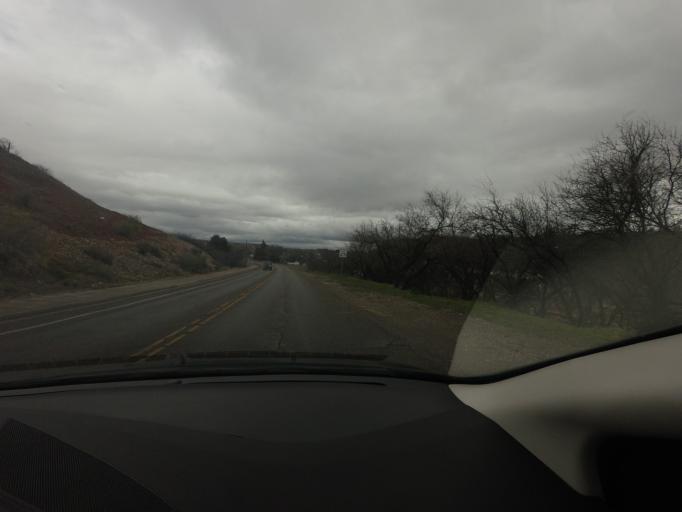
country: US
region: Arizona
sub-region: Yavapai County
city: Cottonwood
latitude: 34.7504
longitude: -112.0310
